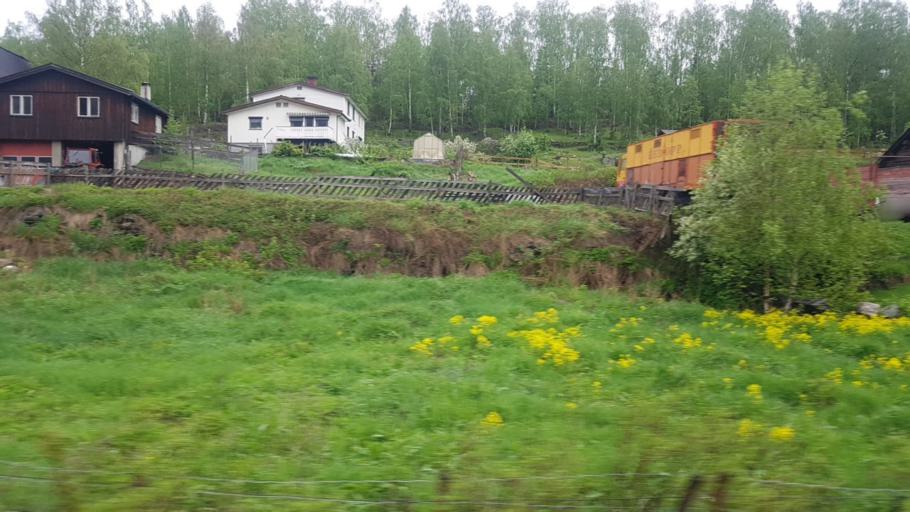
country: NO
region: Oppland
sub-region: Sor-Fron
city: Hundorp
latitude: 61.5654
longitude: 9.9253
